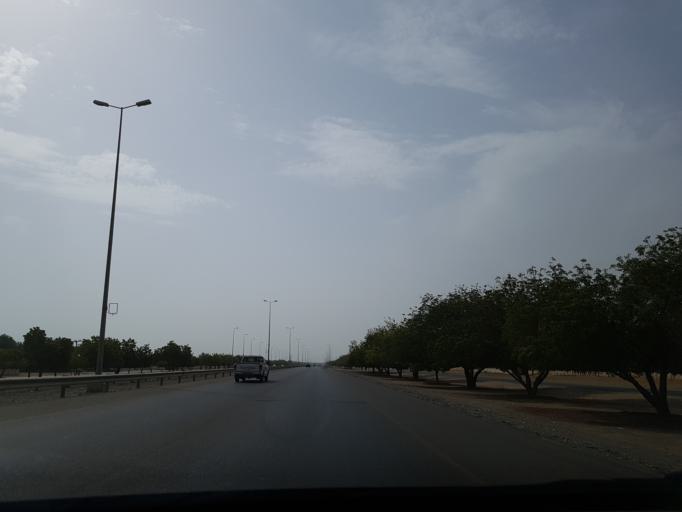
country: OM
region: Al Batinah
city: Saham
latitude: 24.1199
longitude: 56.9047
